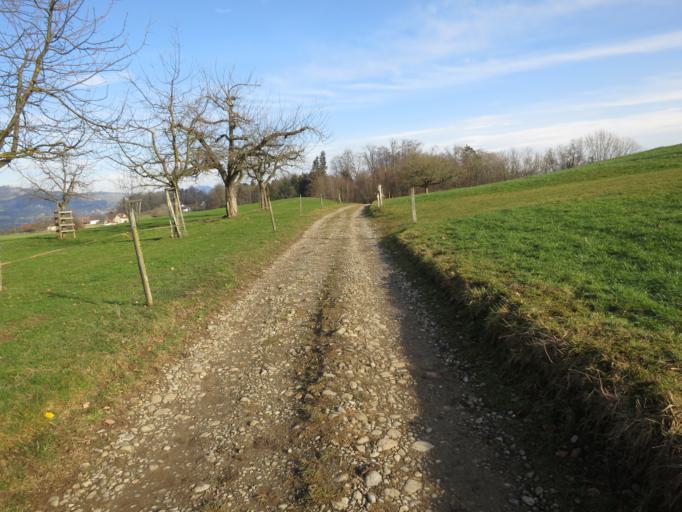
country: CH
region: Zurich
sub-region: Bezirk Hinwil
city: Wolfhausen
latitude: 47.2470
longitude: 8.8061
